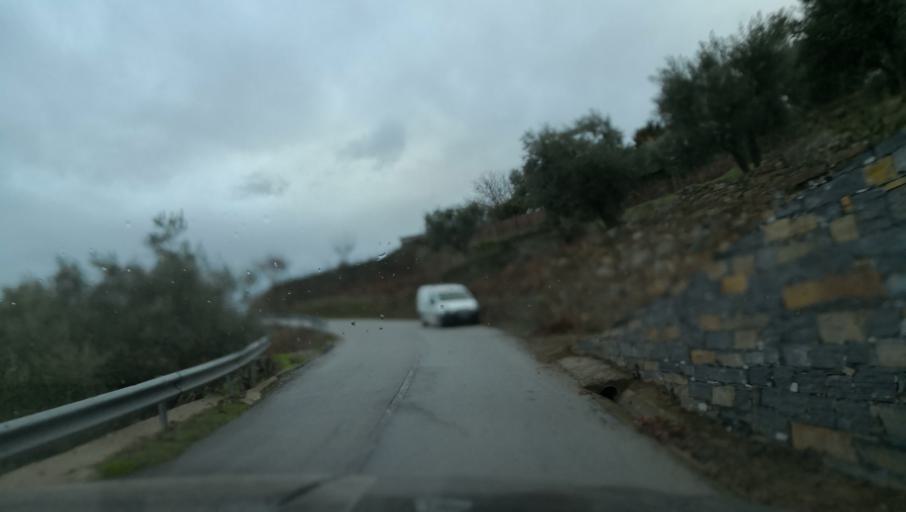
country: PT
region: Vila Real
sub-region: Santa Marta de Penaguiao
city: Santa Marta de Penaguiao
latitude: 41.2035
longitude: -7.7541
